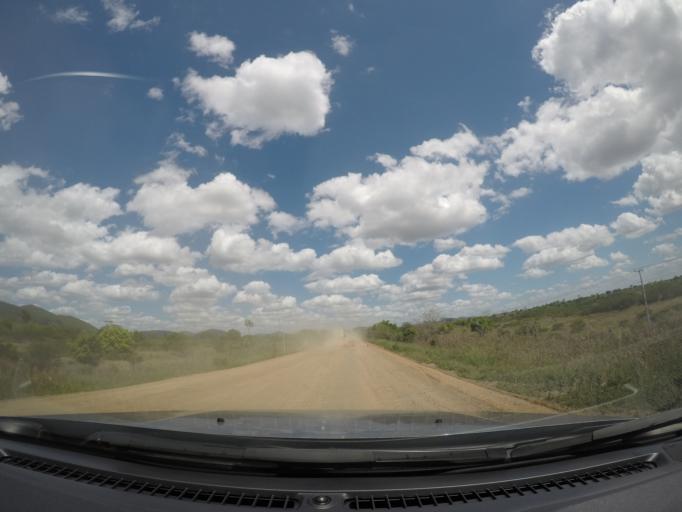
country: BR
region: Bahia
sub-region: Anguera
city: Anguera
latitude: -12.1789
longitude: -39.3963
